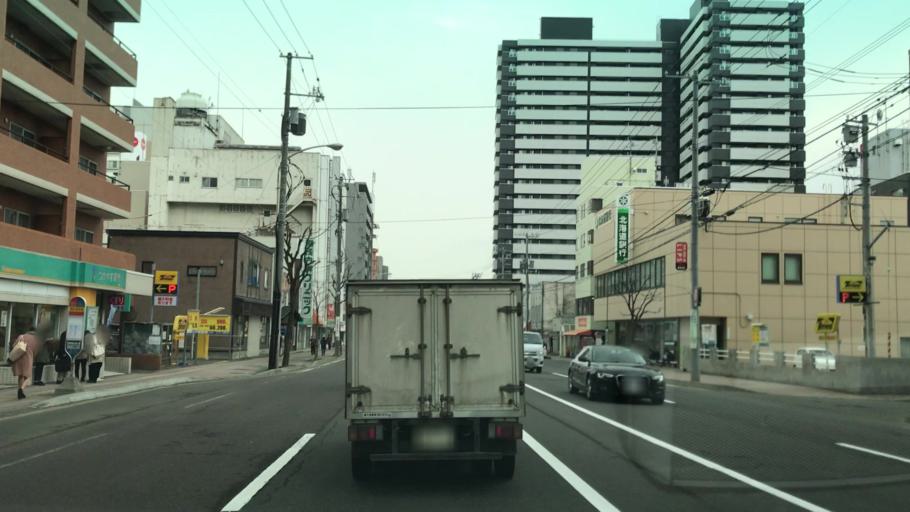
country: JP
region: Hokkaido
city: Sapporo
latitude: 43.0737
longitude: 141.2983
